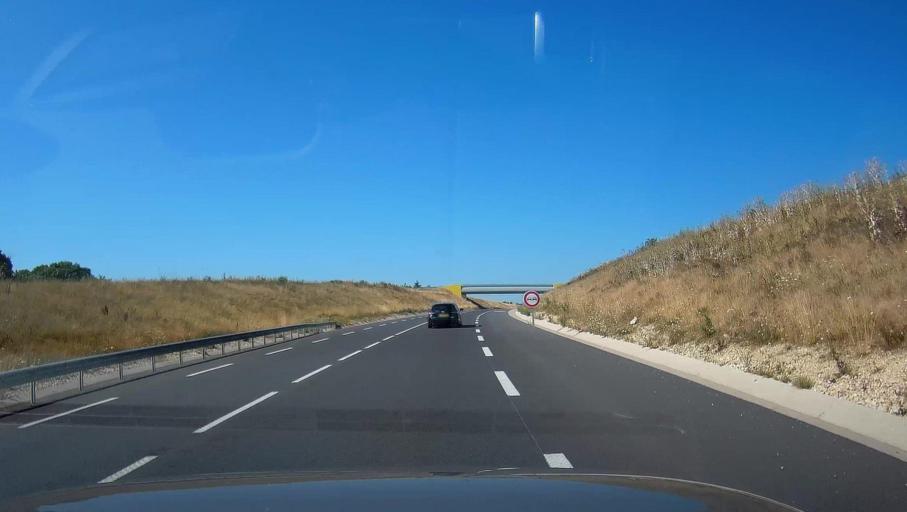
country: FR
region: Lorraine
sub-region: Departement de Meurthe-et-Moselle
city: Colombey-les-Belles
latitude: 48.5483
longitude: 5.9150
